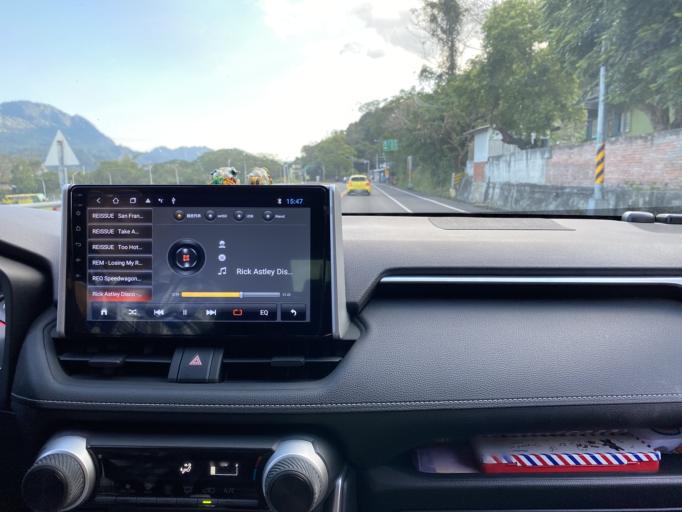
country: TW
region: Taiwan
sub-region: Taitung
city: Taitung
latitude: 22.9079
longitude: 121.1360
